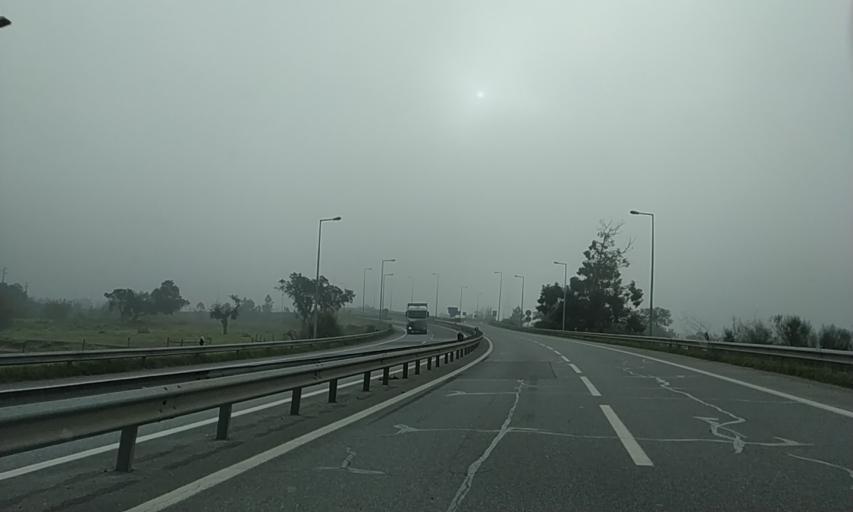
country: PT
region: Setubal
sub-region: Montijo
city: Montijo
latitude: 38.6810
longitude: -8.9476
